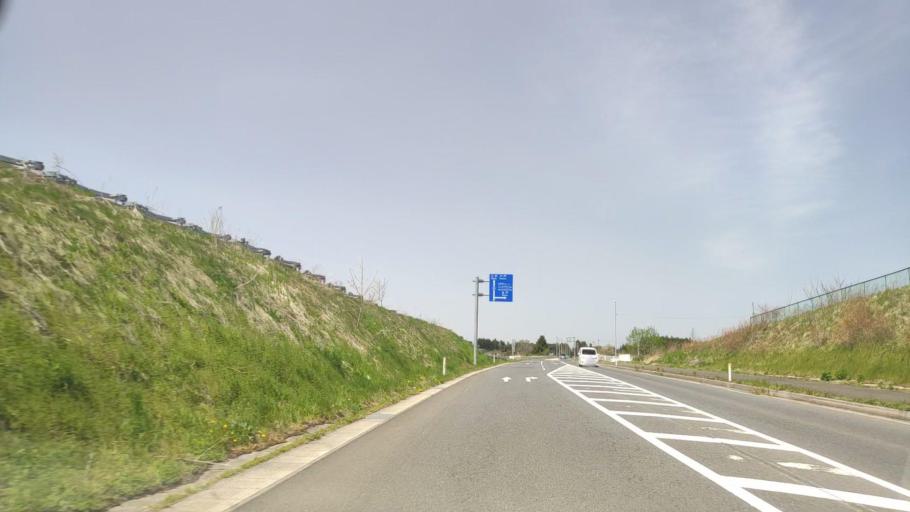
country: JP
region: Aomori
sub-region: Hachinohe Shi
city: Uchimaru
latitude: 40.5273
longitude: 141.4095
